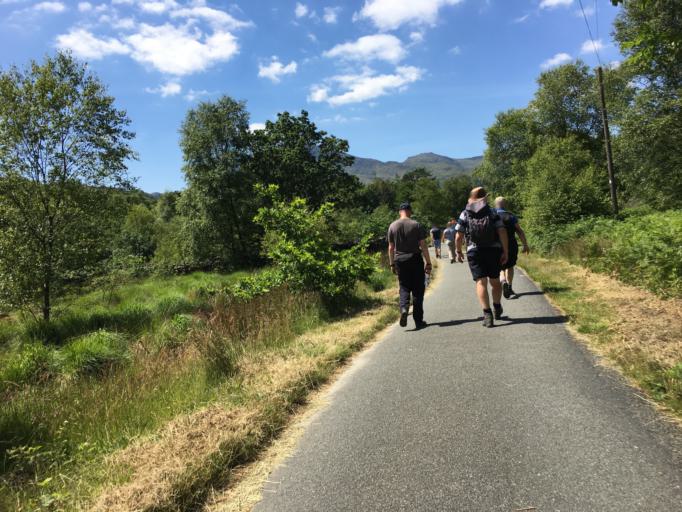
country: GB
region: Wales
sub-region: Gwynedd
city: Penrhyndeudraeth
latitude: 53.0184
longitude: -4.0823
